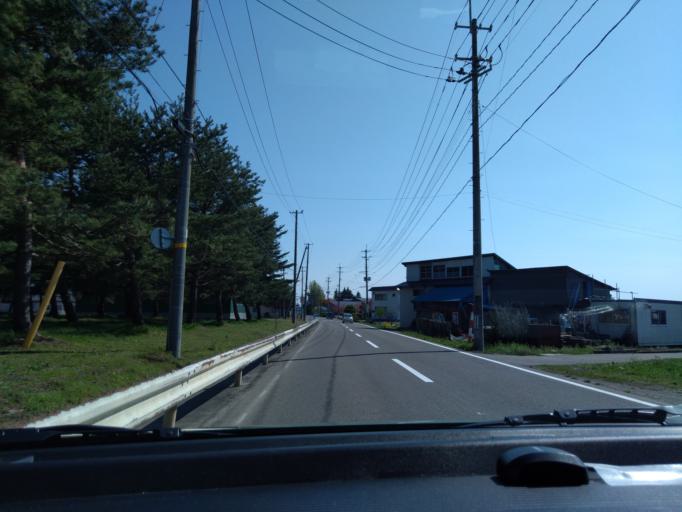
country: JP
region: Akita
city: Omagari
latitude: 39.4634
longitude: 140.5812
